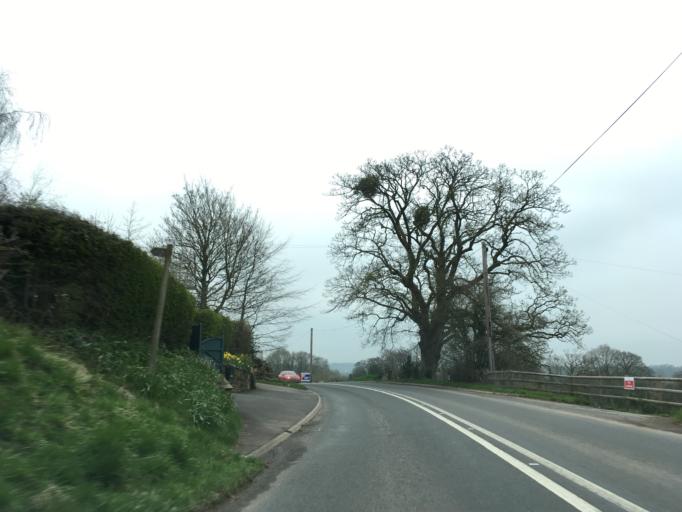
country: GB
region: Wales
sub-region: Monmouthshire
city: Llangybi
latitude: 51.6800
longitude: -2.9056
